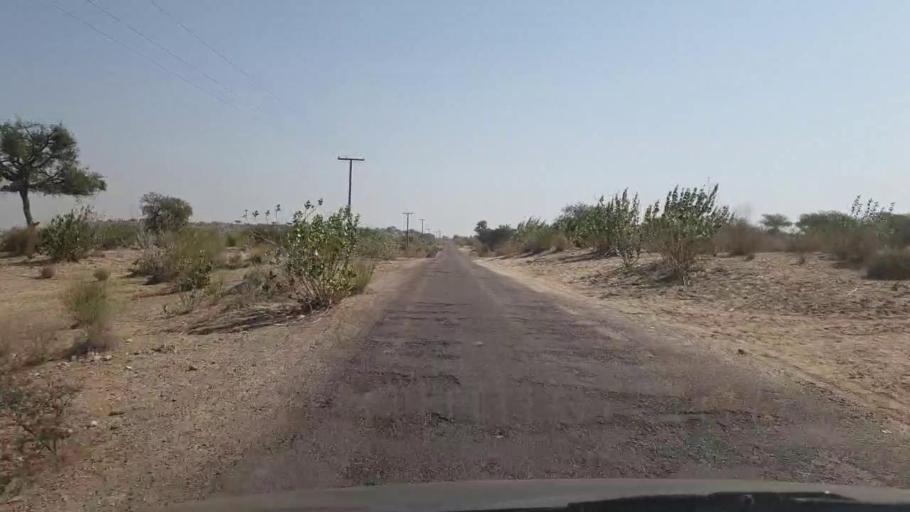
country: PK
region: Sindh
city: Chor
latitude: 25.5948
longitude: 69.9646
